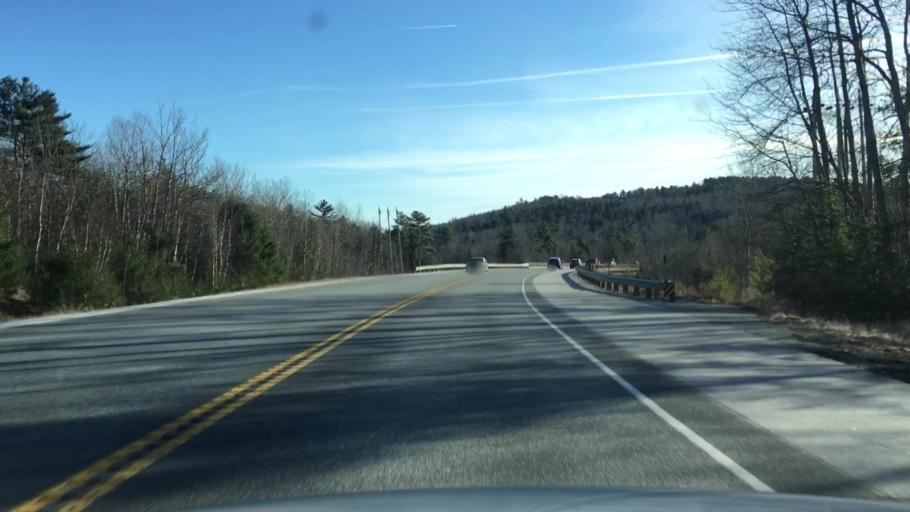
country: US
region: Maine
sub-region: Hancock County
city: Dedham
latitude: 44.6828
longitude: -68.5790
